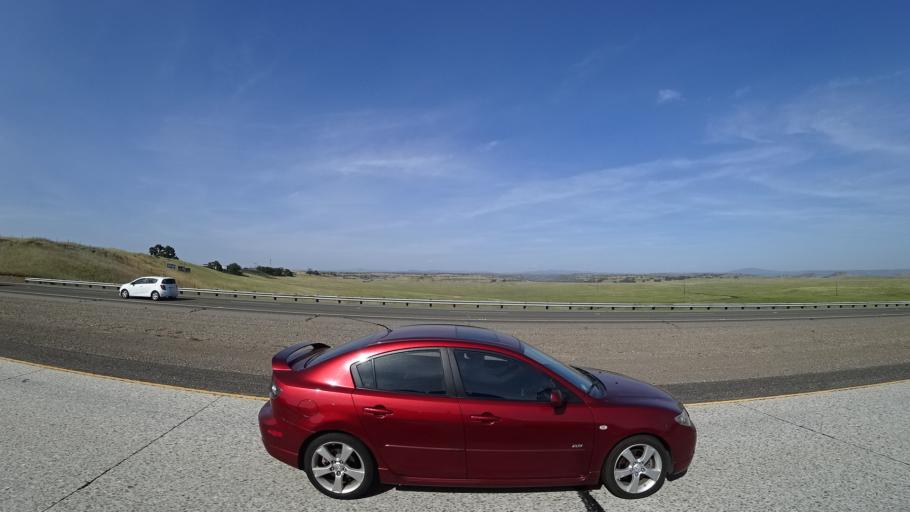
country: US
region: California
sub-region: Butte County
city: Durham
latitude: 39.6594
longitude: -121.7359
